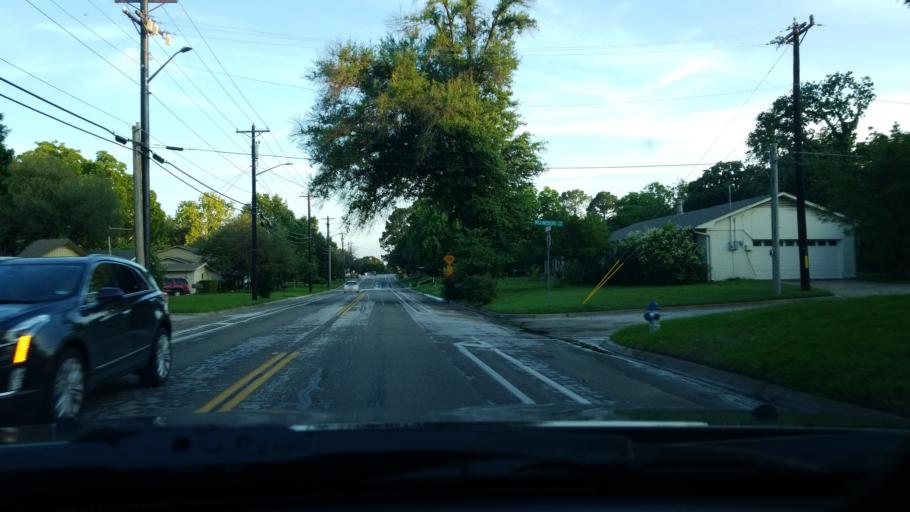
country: US
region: Texas
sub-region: Denton County
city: Denton
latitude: 33.2383
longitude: -97.1067
